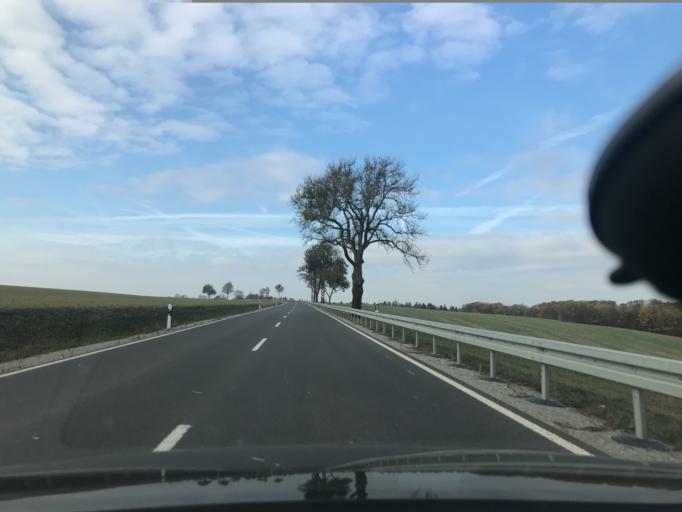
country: DE
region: Thuringia
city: Katharinenberg
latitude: 51.1875
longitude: 10.2750
